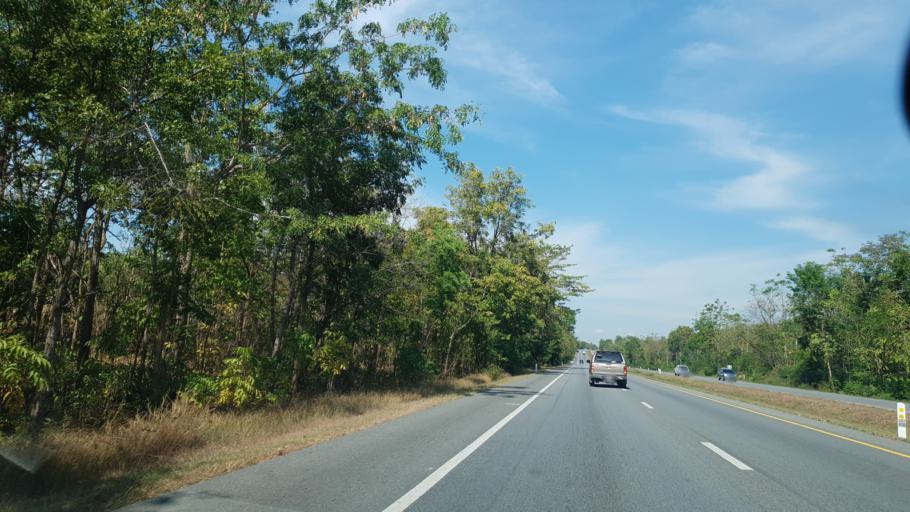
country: TH
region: Uttaradit
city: Thong Saen Khan
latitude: 17.4135
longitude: 100.2282
